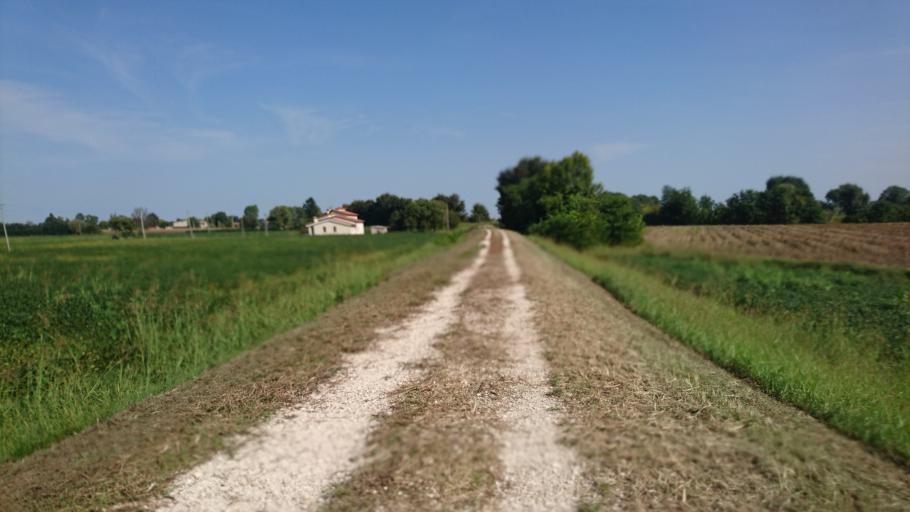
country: IT
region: Veneto
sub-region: Provincia di Padova
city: Saccolongo
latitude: 45.4231
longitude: 11.7379
